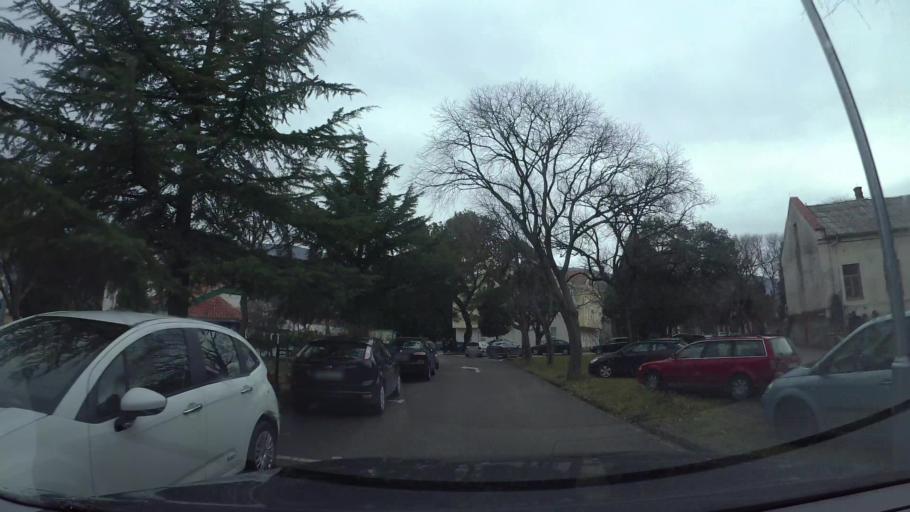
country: BA
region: Federation of Bosnia and Herzegovina
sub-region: Hercegovacko-Bosanski Kanton
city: Mostar
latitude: 43.3533
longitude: 17.8112
